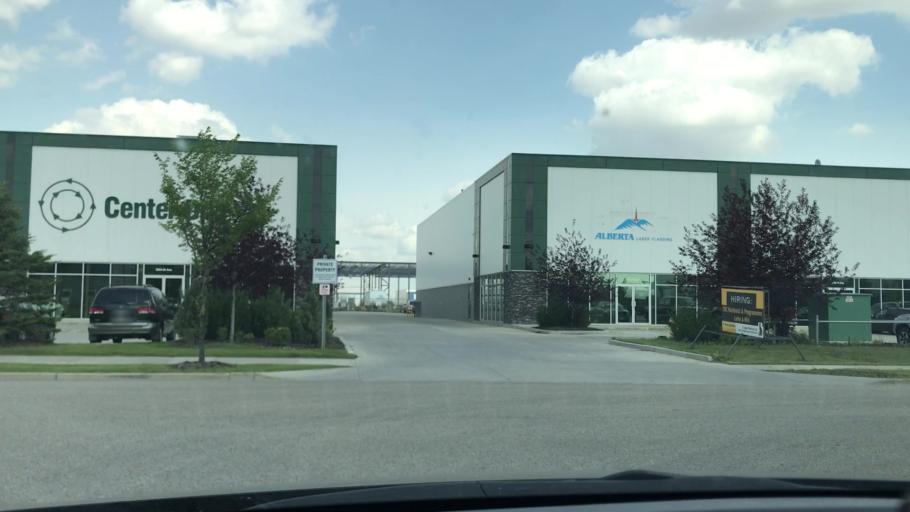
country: CA
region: Alberta
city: Sherwood Park
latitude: 53.4928
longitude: -113.4007
